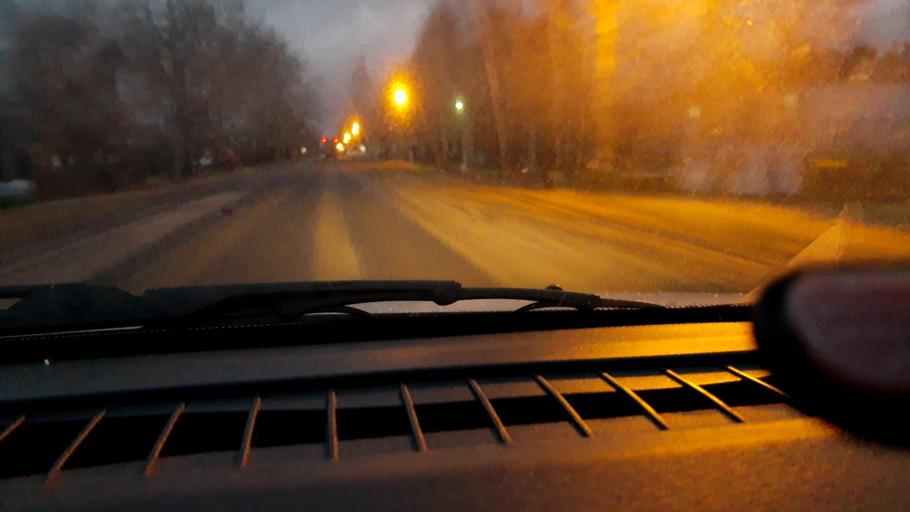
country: RU
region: Nizjnij Novgorod
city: Uren'
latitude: 57.4469
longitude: 45.7379
